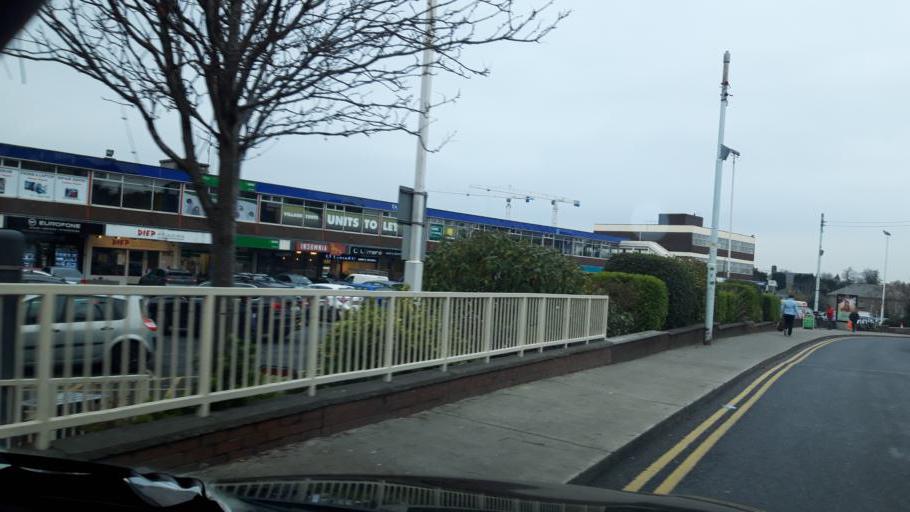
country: IE
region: Leinster
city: Dundrum
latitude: 53.2908
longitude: -6.2453
